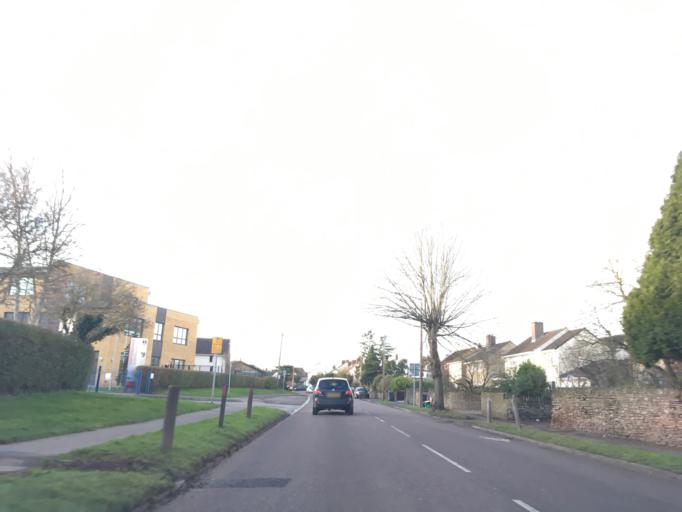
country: GB
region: England
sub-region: South Gloucestershire
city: Winterbourne
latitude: 51.5250
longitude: -2.5075
